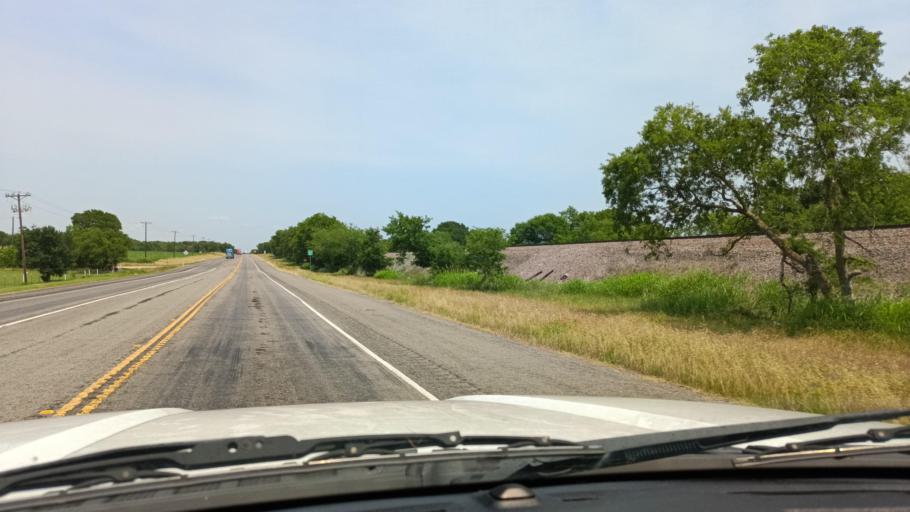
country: US
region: Texas
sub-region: Milam County
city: Cameron
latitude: 30.8487
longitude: -97.0339
